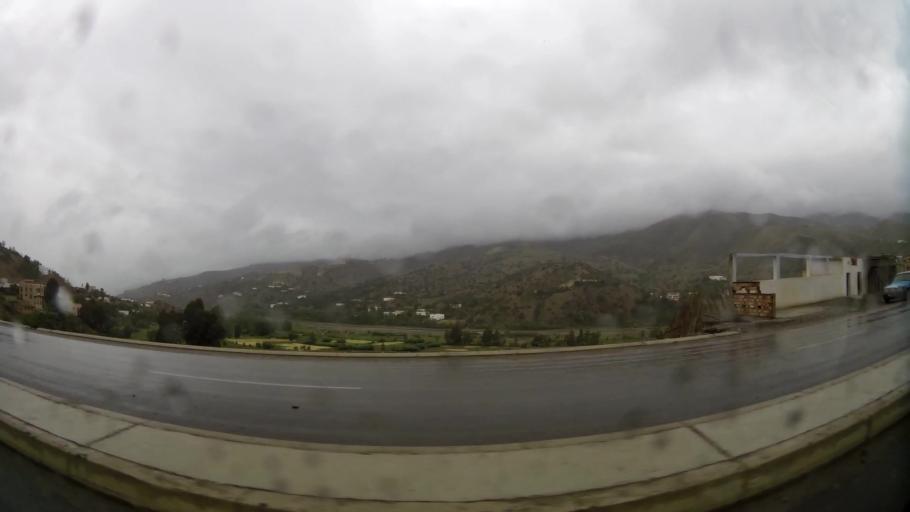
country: MA
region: Taza-Al Hoceima-Taounate
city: Imzourene
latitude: 35.0233
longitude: -3.8221
